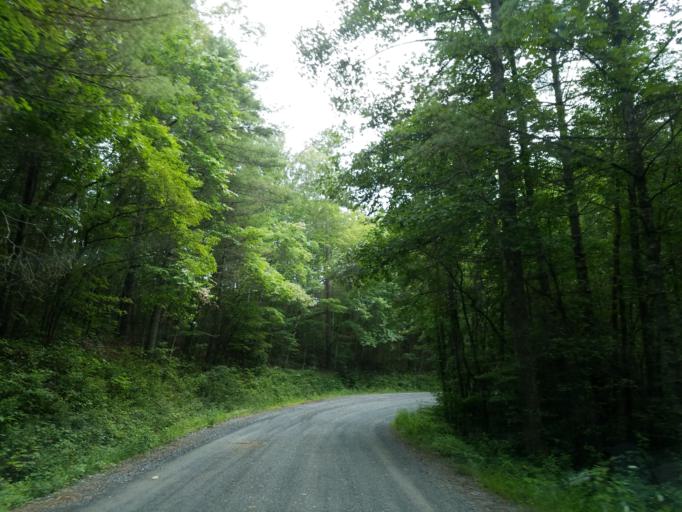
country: US
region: Georgia
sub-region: Fannin County
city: Blue Ridge
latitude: 34.8221
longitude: -84.2311
